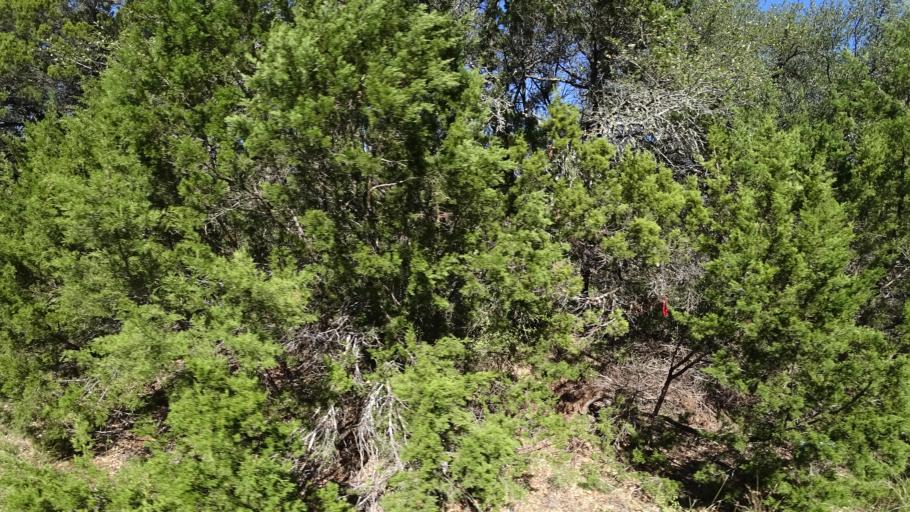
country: US
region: Texas
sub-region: Travis County
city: West Lake Hills
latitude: 30.3067
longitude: -97.8147
